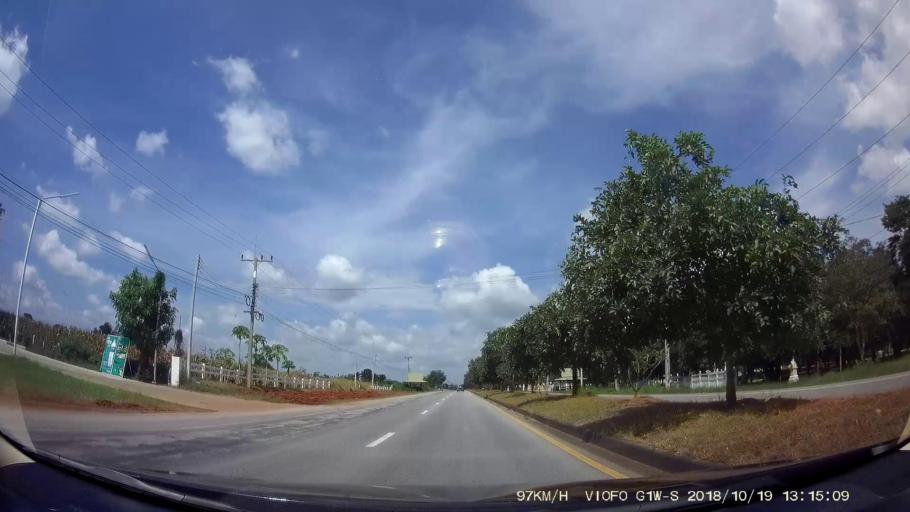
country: TH
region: Chaiyaphum
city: Chatturat
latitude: 15.3857
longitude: 101.8376
